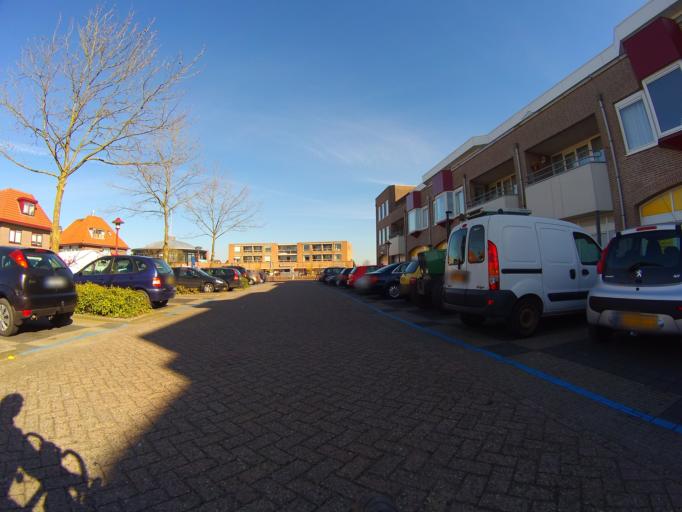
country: NL
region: Utrecht
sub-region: Gemeente Utrechtse Heuvelrug
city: Overberg
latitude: 52.0807
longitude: 5.4892
